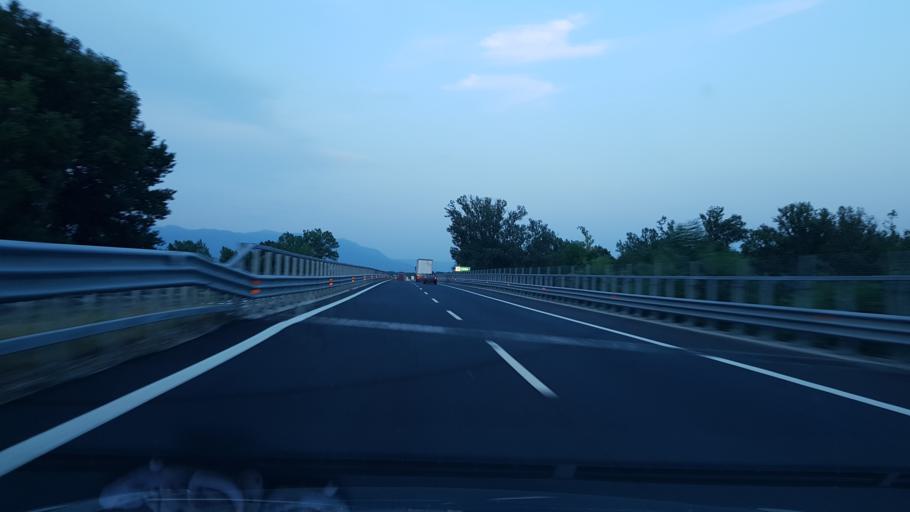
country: IT
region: Friuli Venezia Giulia
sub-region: Provincia di Gorizia
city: Savogna d'Isonzo
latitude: 45.9038
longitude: 13.5549
